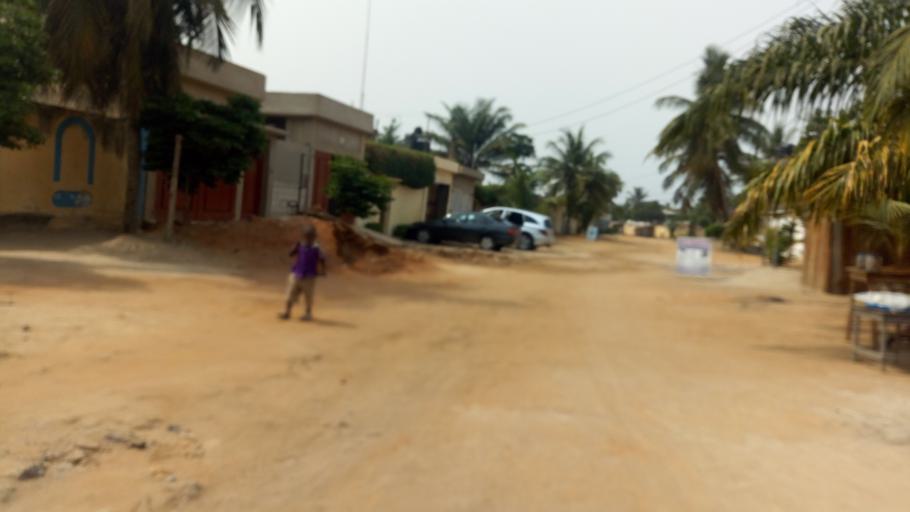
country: TG
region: Maritime
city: Lome
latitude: 6.1750
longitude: 1.1737
